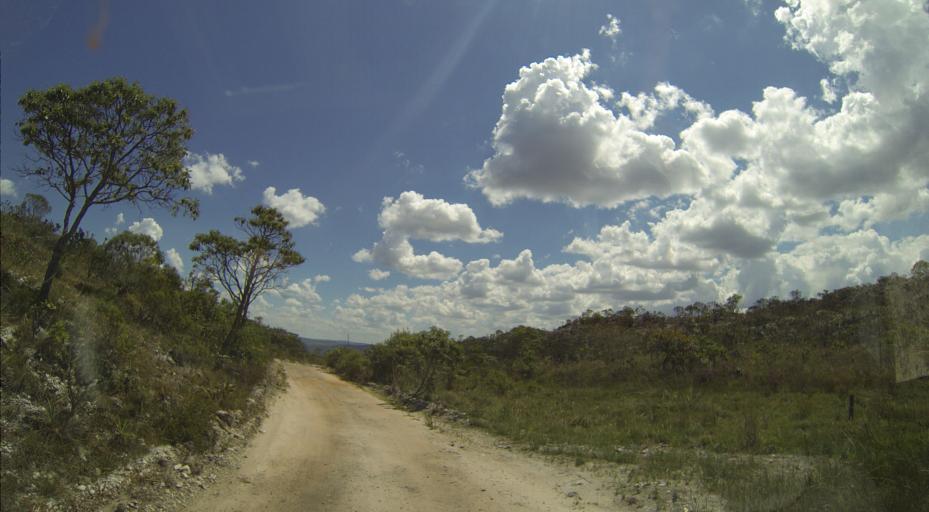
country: BR
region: Minas Gerais
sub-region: Serro
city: Serro
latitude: -18.4629
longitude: -43.4517
